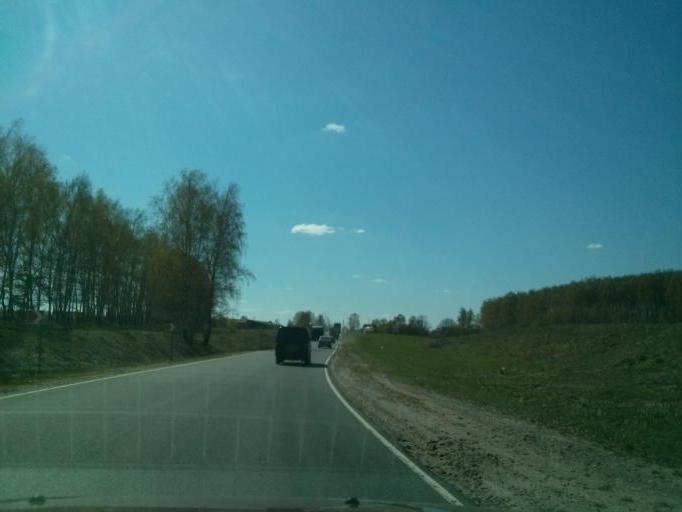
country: RU
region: Nizjnij Novgorod
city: Vorsma
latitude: 56.0413
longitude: 43.3826
